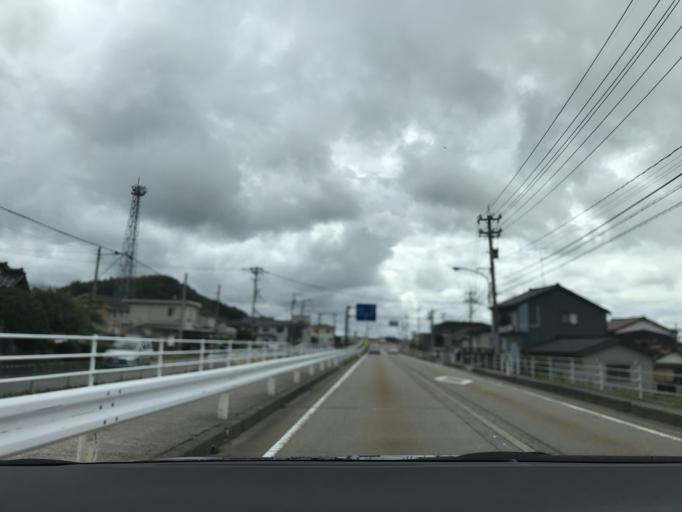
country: JP
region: Ishikawa
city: Tsubata
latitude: 36.6567
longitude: 136.7287
